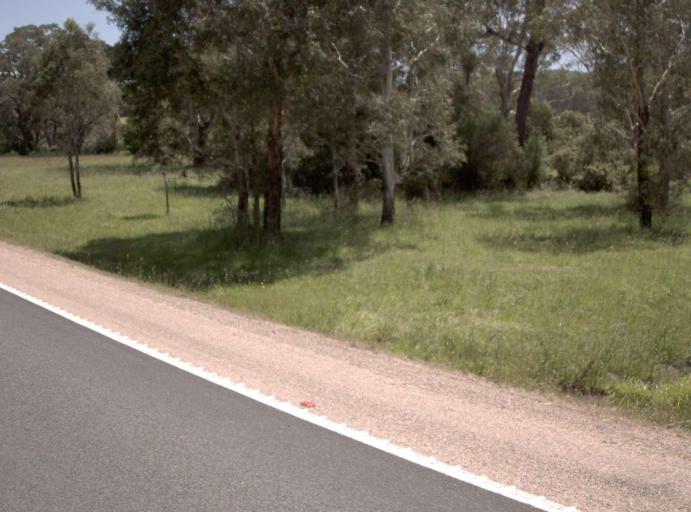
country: AU
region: Victoria
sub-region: East Gippsland
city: Bairnsdale
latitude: -37.7515
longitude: 147.7277
